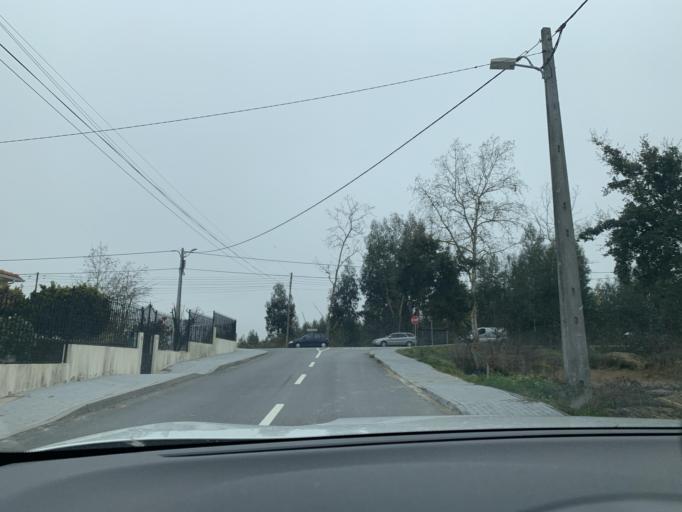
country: PT
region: Viseu
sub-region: Concelho de Tondela
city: Tondela
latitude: 40.5349
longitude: -8.0533
